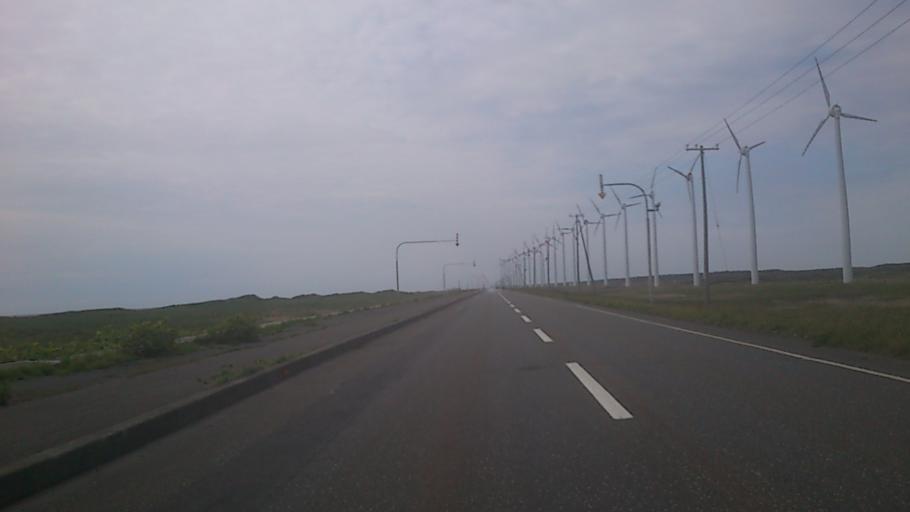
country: JP
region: Hokkaido
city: Makubetsu
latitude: 44.9588
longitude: 141.7051
